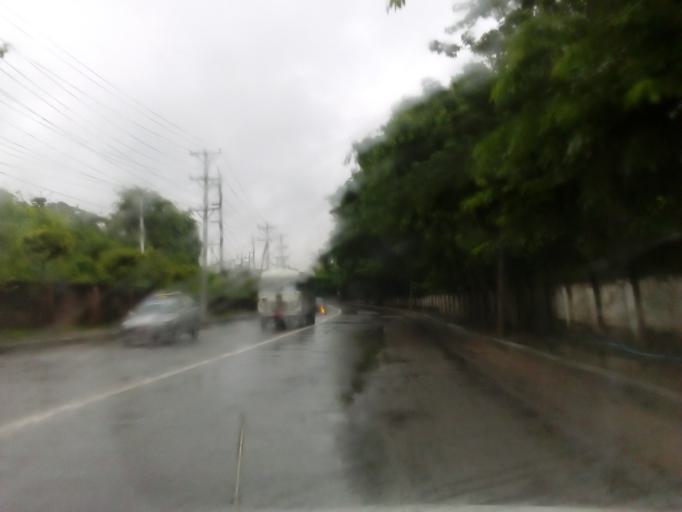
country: MM
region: Yangon
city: Yangon
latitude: 16.8250
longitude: 96.1704
